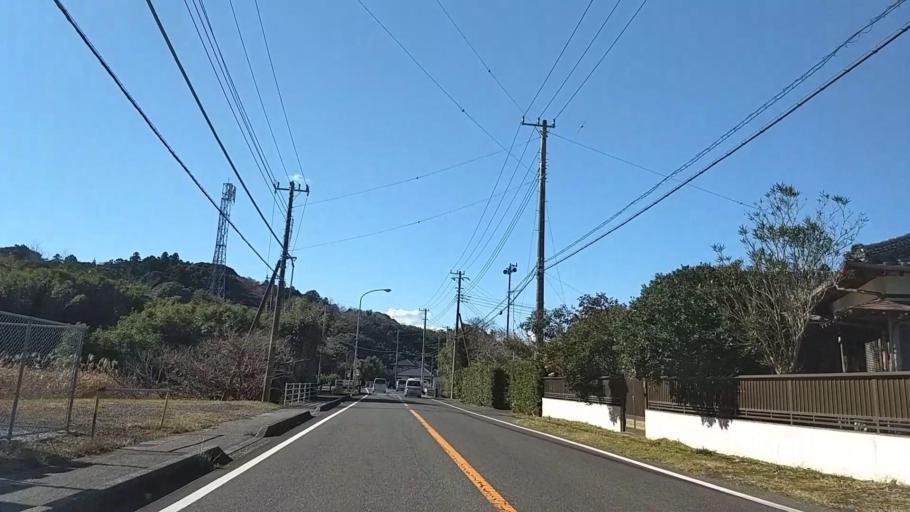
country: JP
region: Chiba
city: Tateyama
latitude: 34.9523
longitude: 139.8397
